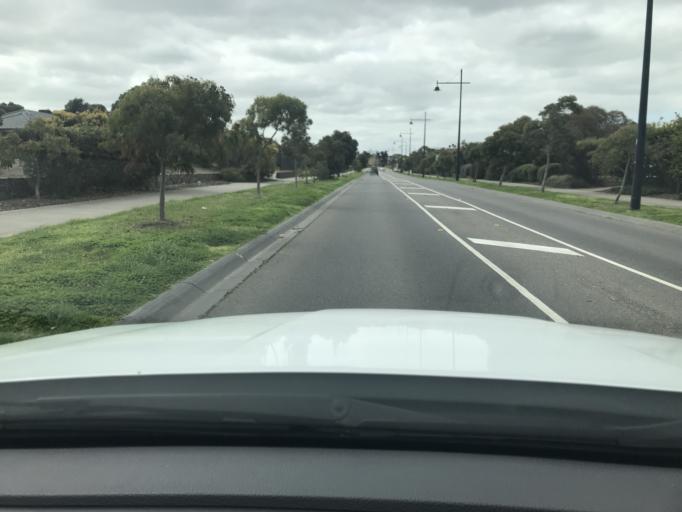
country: AU
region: Victoria
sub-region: Hume
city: Craigieburn
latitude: -37.5794
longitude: 144.9269
